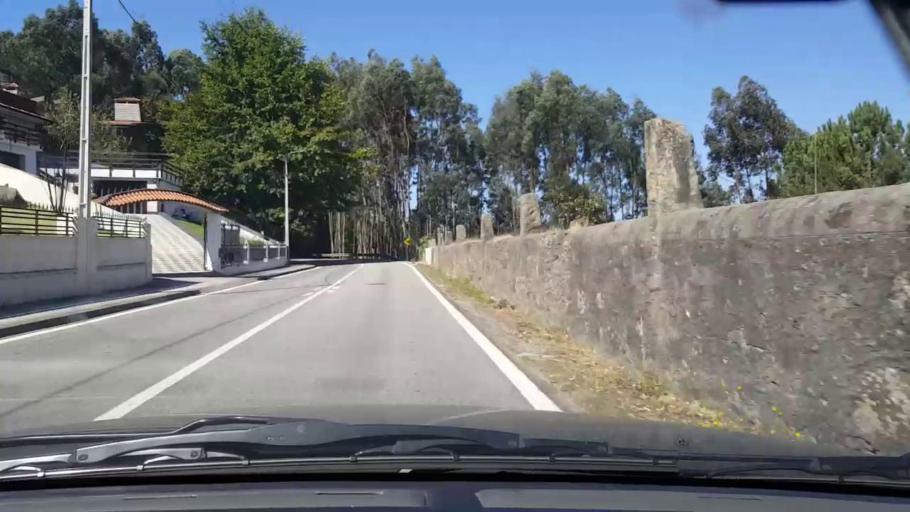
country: PT
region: Porto
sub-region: Vila do Conde
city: Arvore
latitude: 41.3401
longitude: -8.6479
